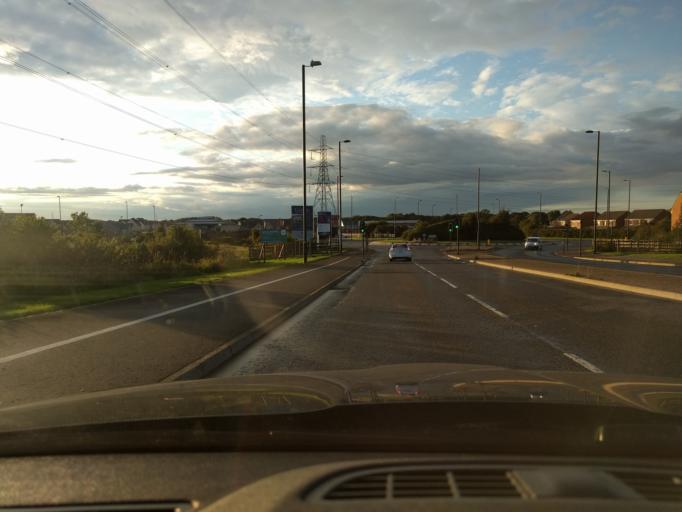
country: GB
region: England
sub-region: Northumberland
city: Backworth
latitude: 55.0333
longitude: -1.5223
